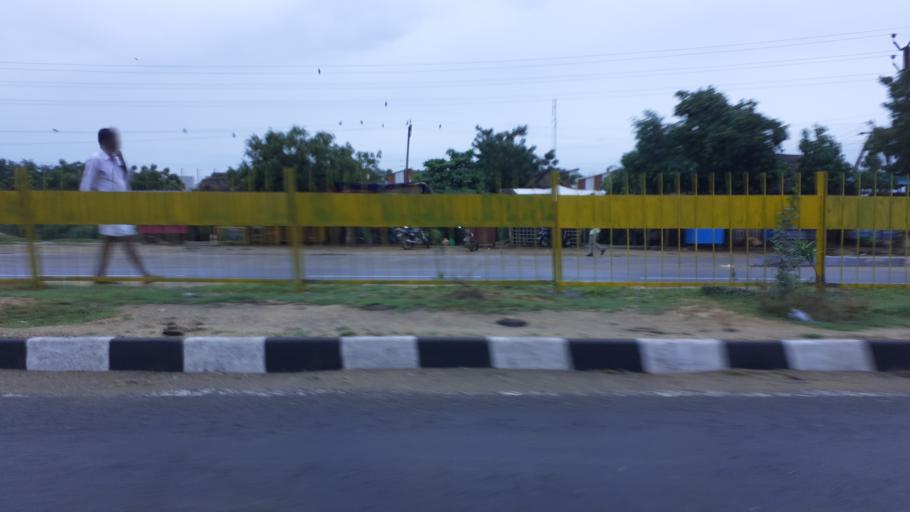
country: IN
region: Tamil Nadu
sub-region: Tirunelveli Kattabo
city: Tirunelveli
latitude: 8.7140
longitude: 77.7708
